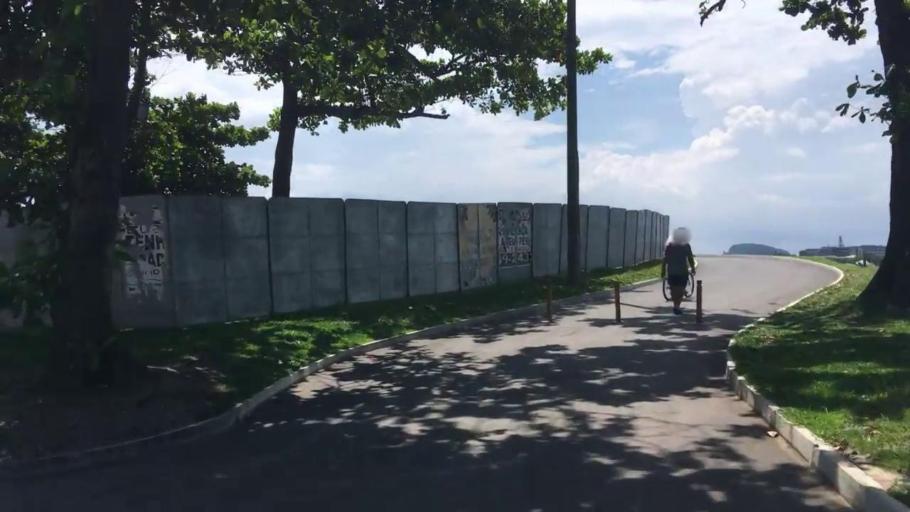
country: BR
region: Rio de Janeiro
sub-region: Rio De Janeiro
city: Rio de Janeiro
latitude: -22.9209
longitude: -43.1684
